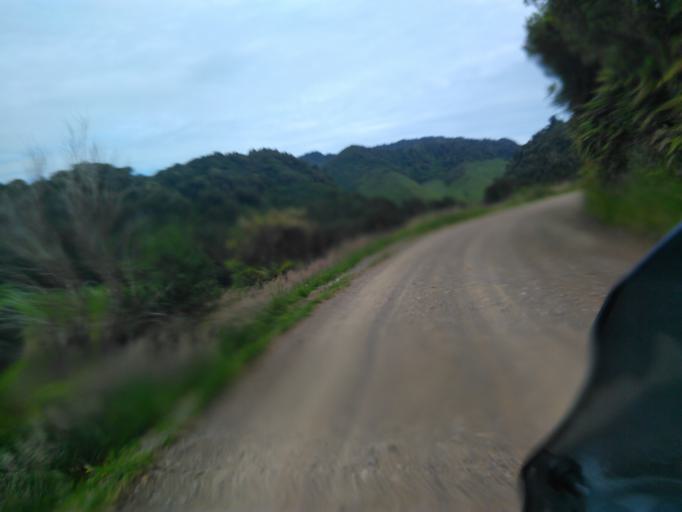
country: NZ
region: Bay of Plenty
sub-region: Opotiki District
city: Opotiki
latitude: -38.1030
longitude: 177.4901
